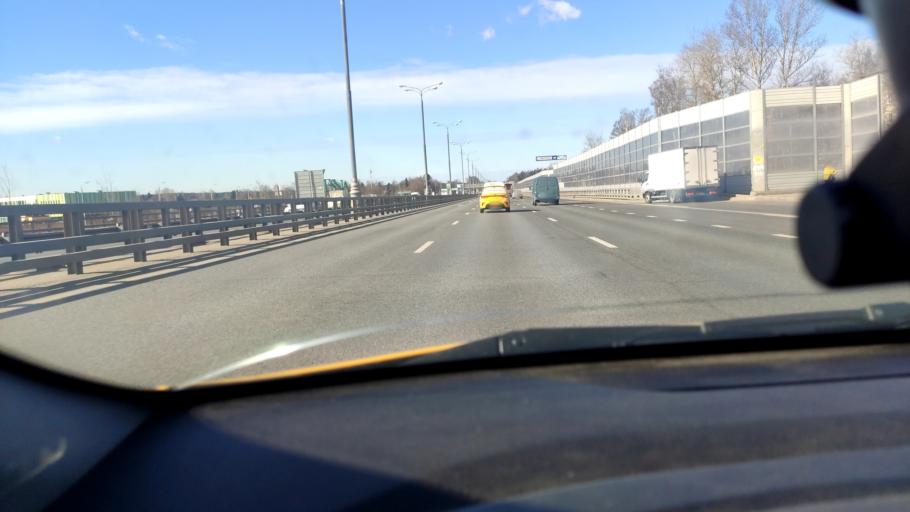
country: RU
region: Moskovskaya
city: Aprelevka
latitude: 55.5348
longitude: 37.0650
